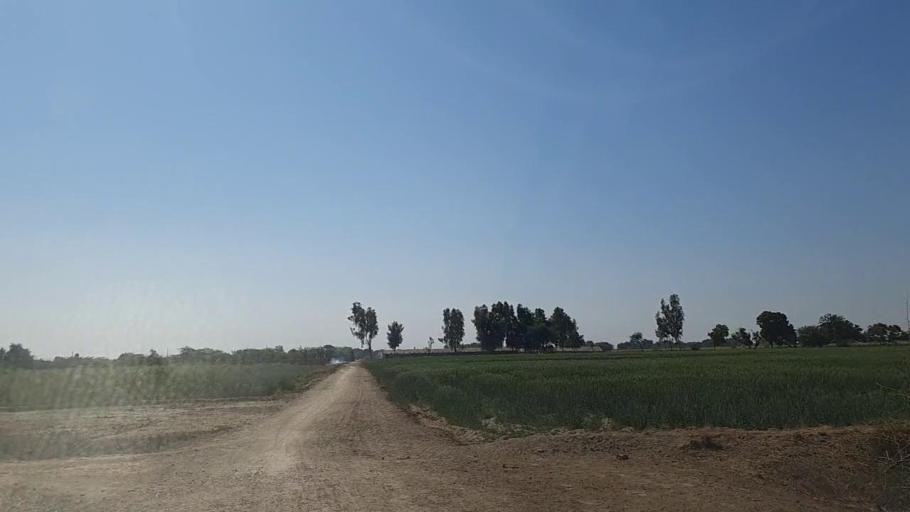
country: PK
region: Sindh
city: Kunri
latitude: 25.2866
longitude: 69.5386
